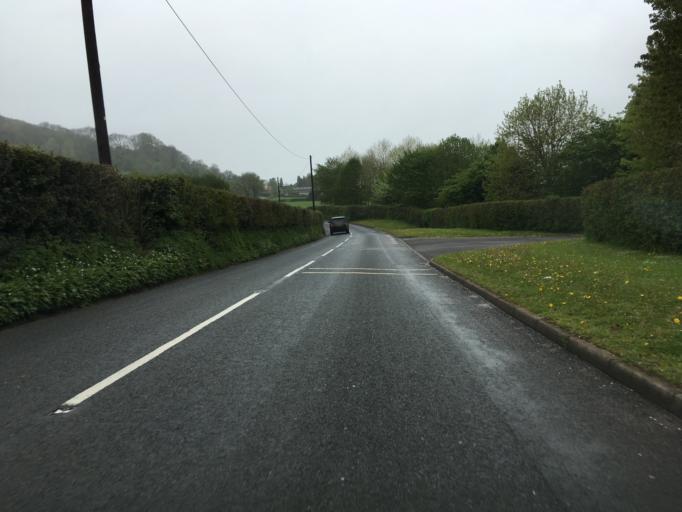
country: GB
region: England
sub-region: Bath and North East Somerset
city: Compton Martin
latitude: 51.3136
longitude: -2.6662
